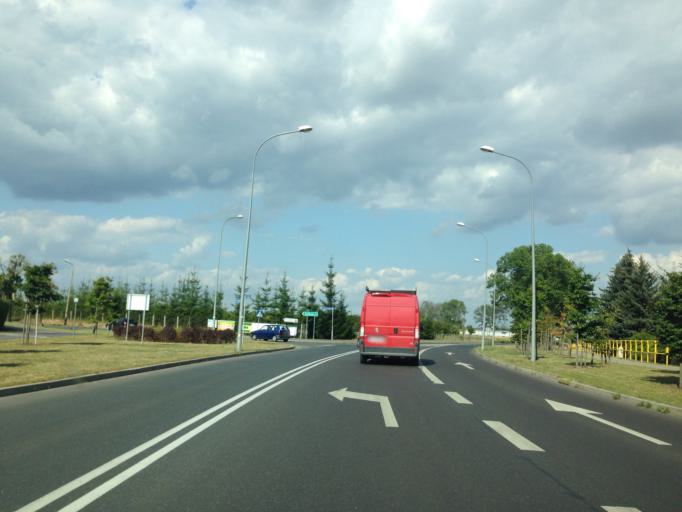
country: PL
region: Warmian-Masurian Voivodeship
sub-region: Powiat ilawski
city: Ilawa
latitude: 53.6103
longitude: 19.5702
